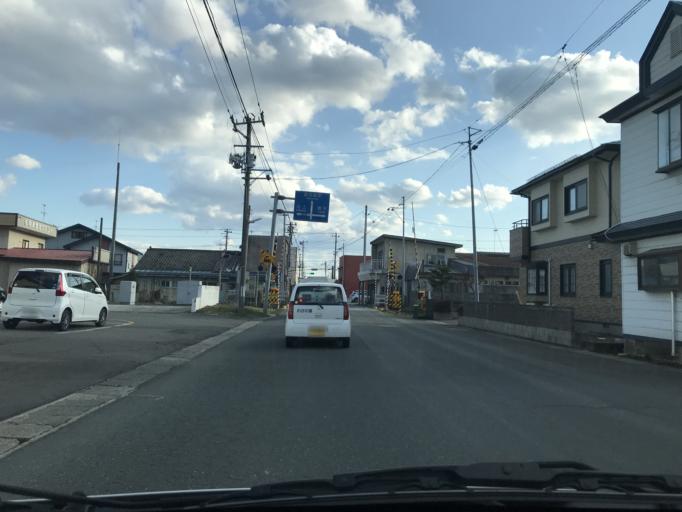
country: JP
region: Iwate
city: Kitakami
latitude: 39.3024
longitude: 141.0331
